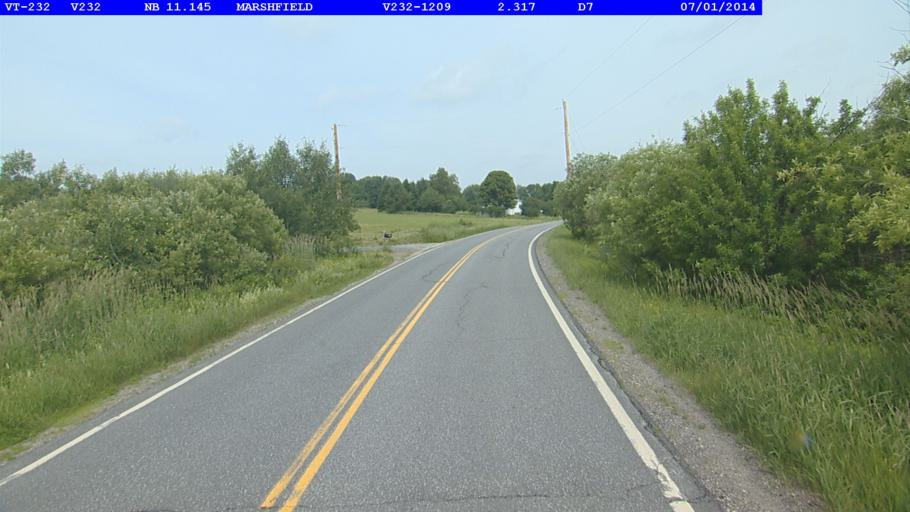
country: US
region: Vermont
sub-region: Caledonia County
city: Hardwick
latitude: 44.3409
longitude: -72.2940
